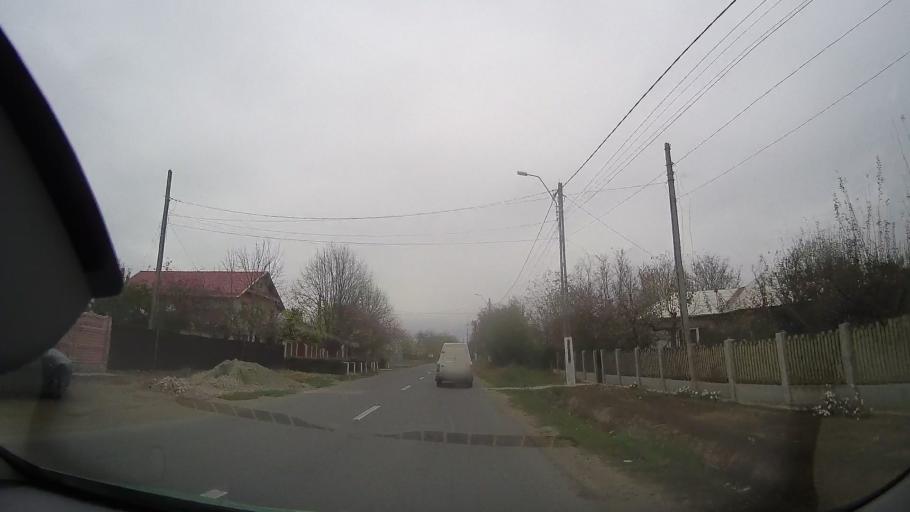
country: RO
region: Braila
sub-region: Comuna Budesti
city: Tataru
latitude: 44.8540
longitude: 27.4229
